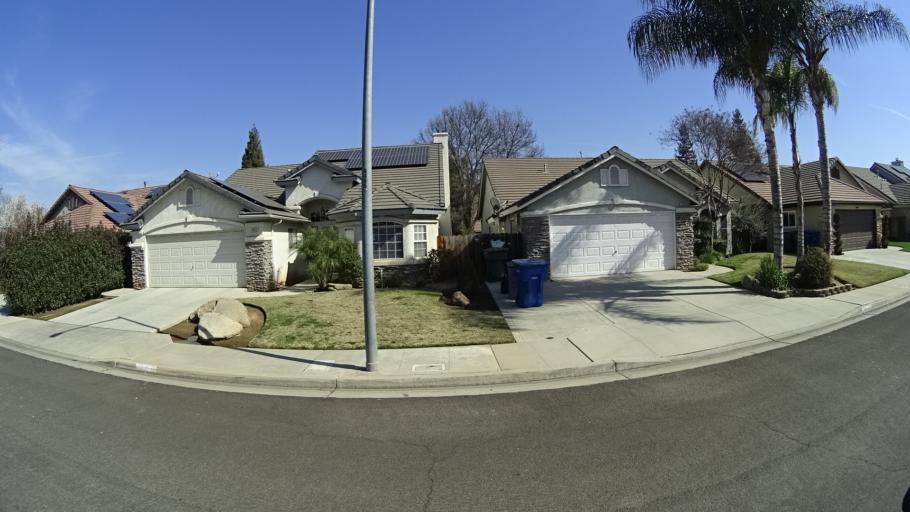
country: US
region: California
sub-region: Fresno County
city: Clovis
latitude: 36.8876
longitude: -119.7444
